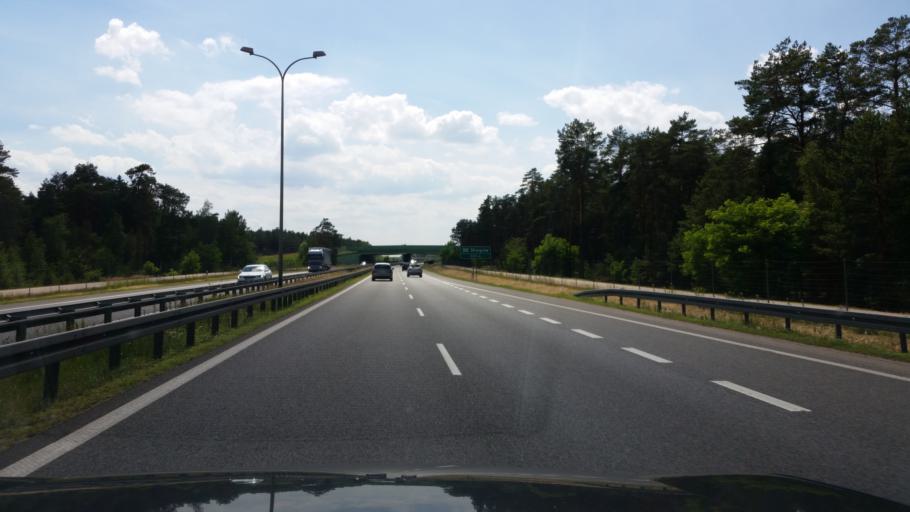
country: PL
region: Masovian Voivodeship
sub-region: Powiat wyszkowski
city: Wyszkow
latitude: 52.5186
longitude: 21.4061
